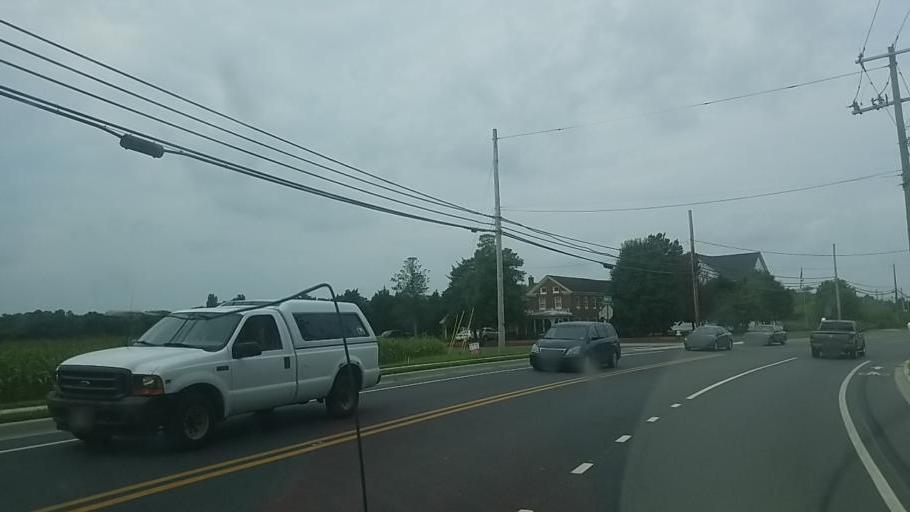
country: US
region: Delaware
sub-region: Sussex County
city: Ocean View
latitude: 38.5475
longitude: -75.1122
